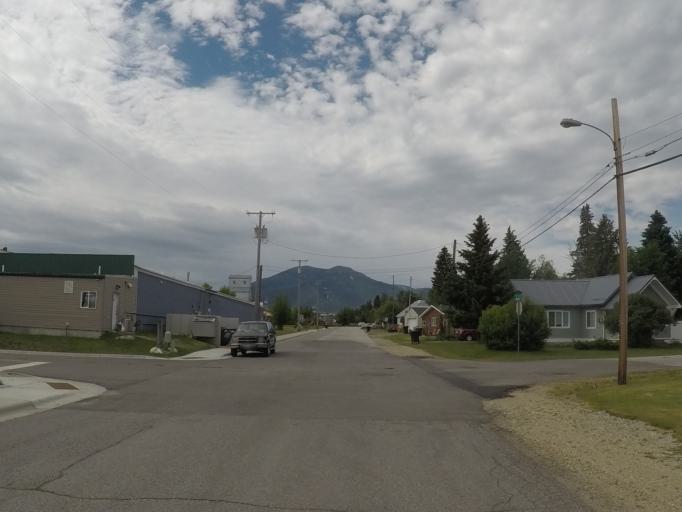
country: US
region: Montana
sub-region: Carbon County
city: Red Lodge
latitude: 45.1940
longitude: -109.2474
